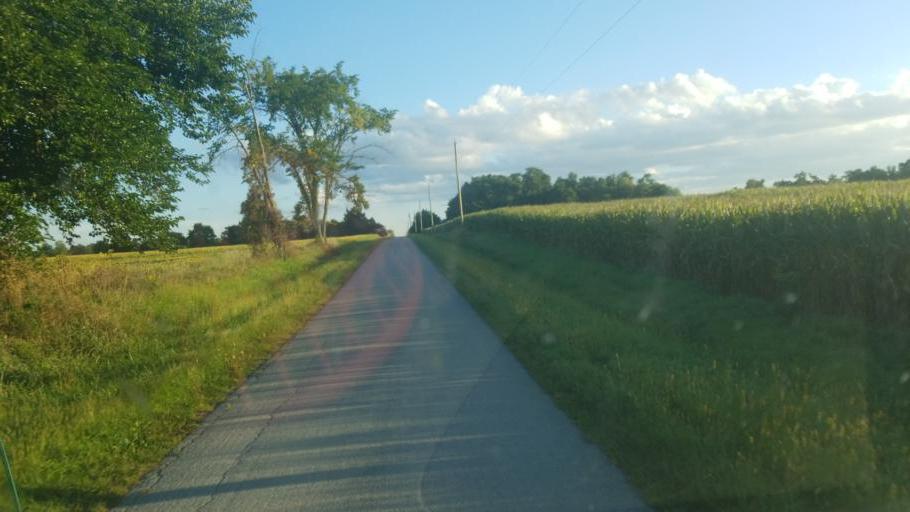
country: US
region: Ohio
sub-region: Wyandot County
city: Upper Sandusky
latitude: 40.8543
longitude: -83.1507
